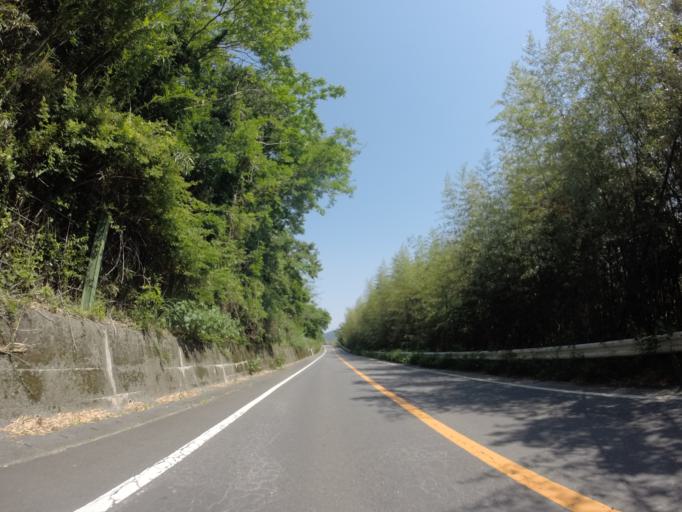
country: JP
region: Shizuoka
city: Fujinomiya
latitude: 35.1988
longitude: 138.5791
